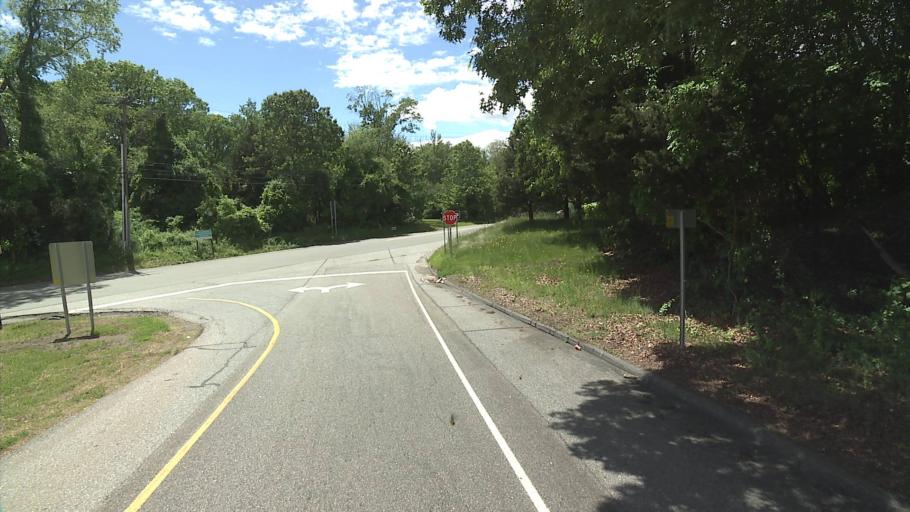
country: US
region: Connecticut
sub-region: Middlesex County
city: Saybrook Manor
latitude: 41.2992
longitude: -72.3931
